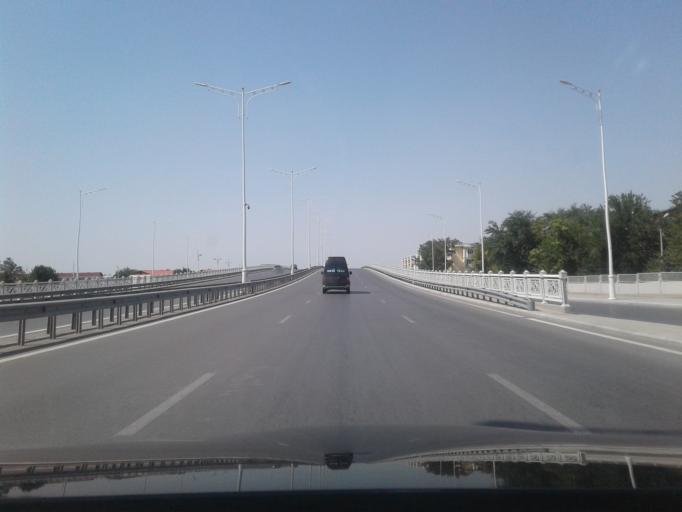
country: TM
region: Ahal
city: Ashgabat
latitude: 37.9162
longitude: 58.4234
